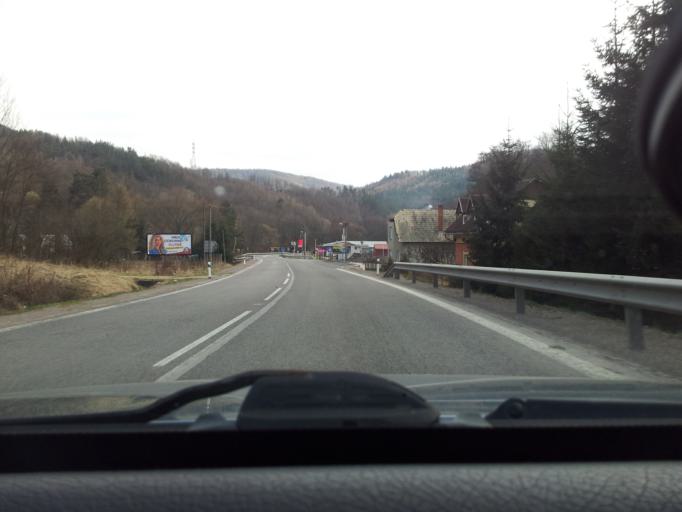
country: SK
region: Banskobystricky
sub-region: Okres Ziar nad Hronom
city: Kremnica
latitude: 48.6879
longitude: 18.9168
